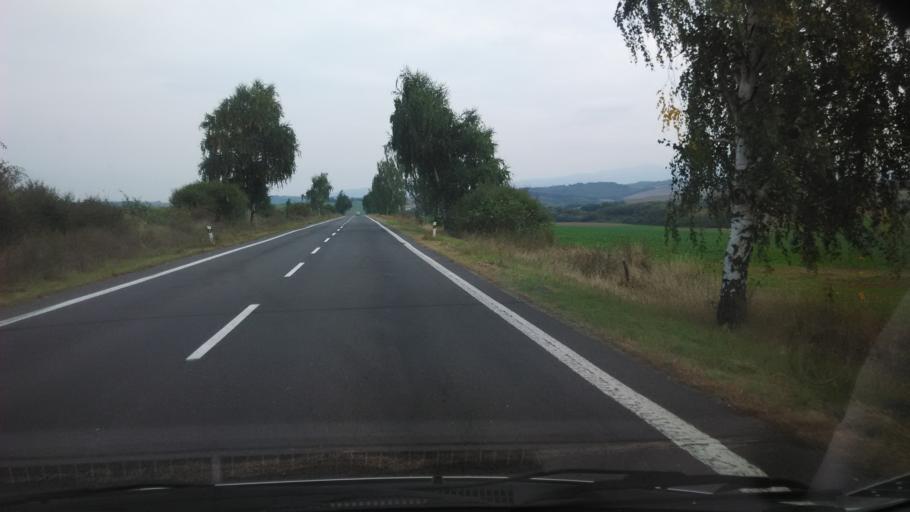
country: SK
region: Nitriansky
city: Zeliezovce
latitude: 48.1261
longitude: 18.7343
